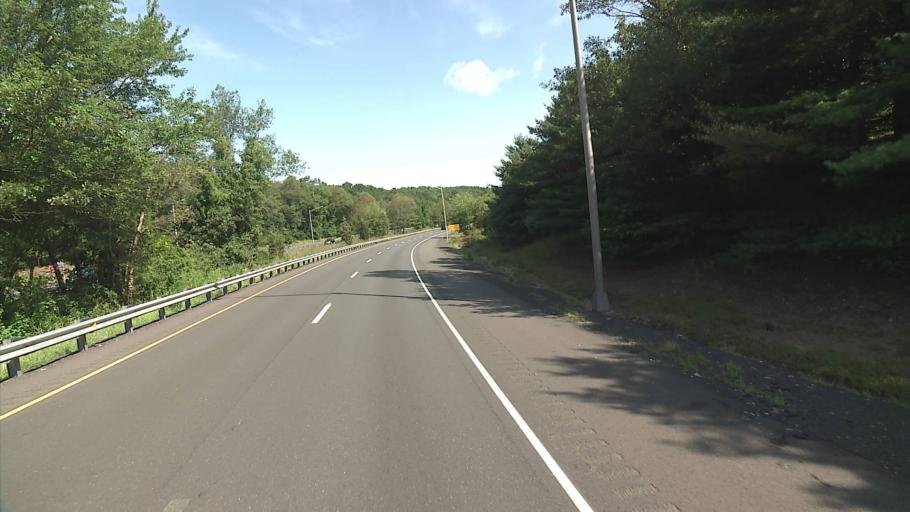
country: US
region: Connecticut
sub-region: Hartford County
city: Glastonbury Center
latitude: 41.6785
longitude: -72.5412
